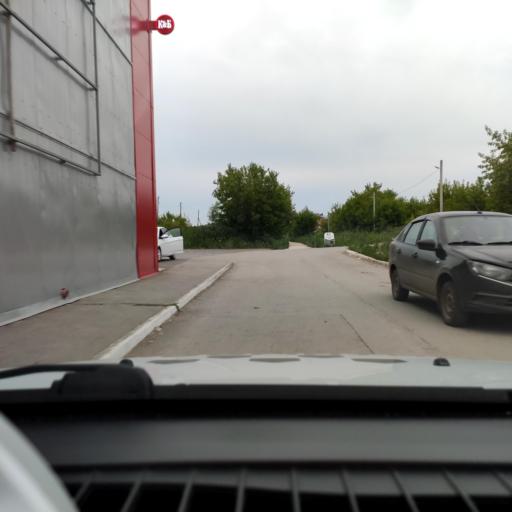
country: RU
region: Perm
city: Ferma
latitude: 57.8970
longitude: 56.3195
